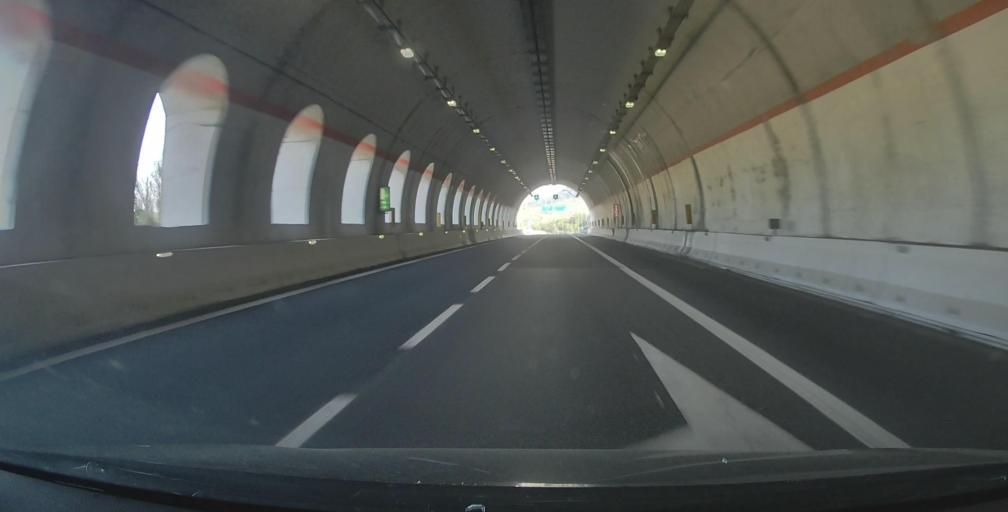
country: IT
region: Basilicate
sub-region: Provincia di Potenza
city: Lagonegro
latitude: 40.1485
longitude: 15.7518
